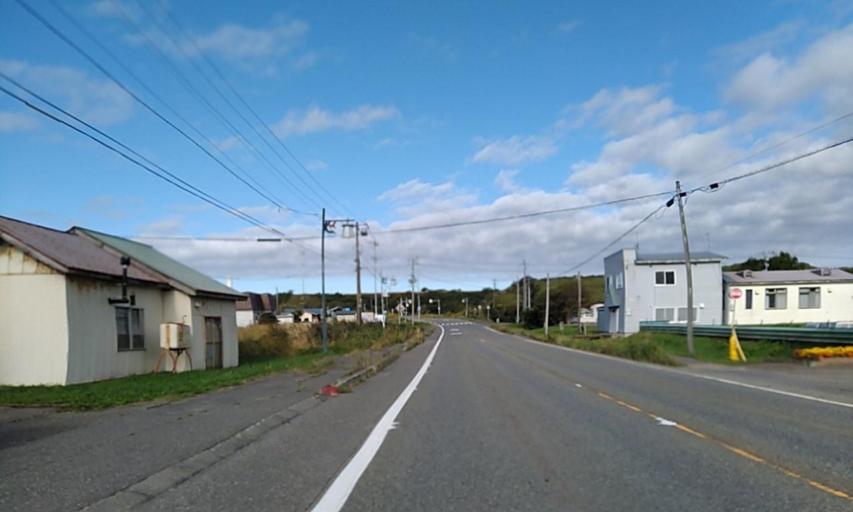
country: JP
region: Hokkaido
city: Shizunai-furukawacho
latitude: 42.2461
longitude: 142.5772
